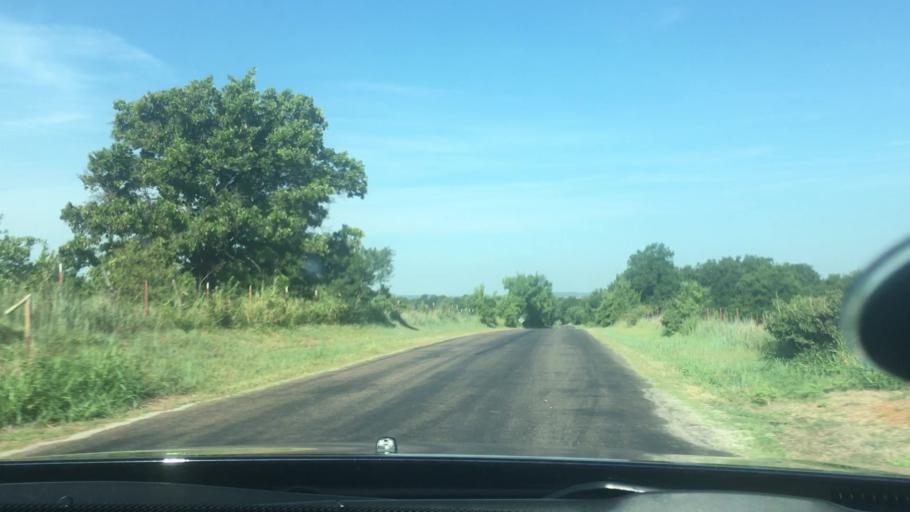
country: US
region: Oklahoma
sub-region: Garvin County
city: Maysville
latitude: 34.6521
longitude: -97.3878
